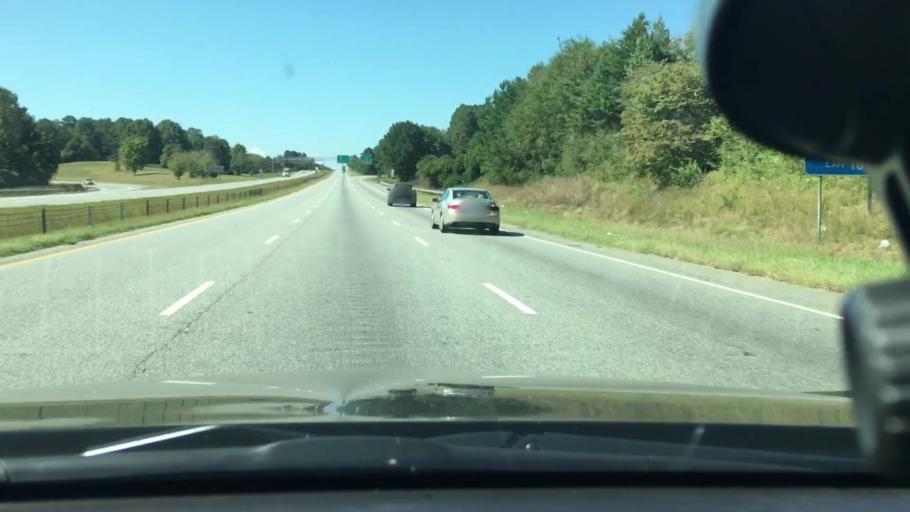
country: US
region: North Carolina
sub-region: Rutherford County
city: Forest City
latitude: 35.3147
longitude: -81.8659
